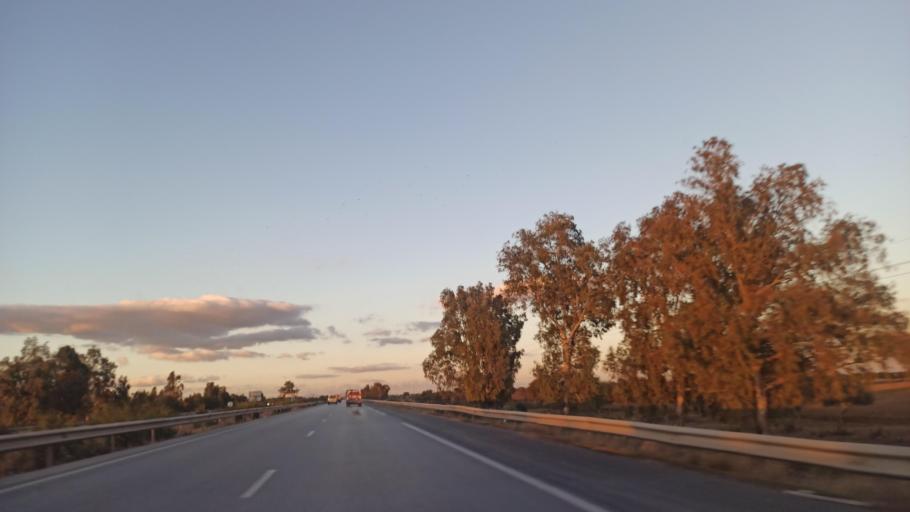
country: TN
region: Susah
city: Harqalah
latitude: 36.1257
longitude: 10.4062
